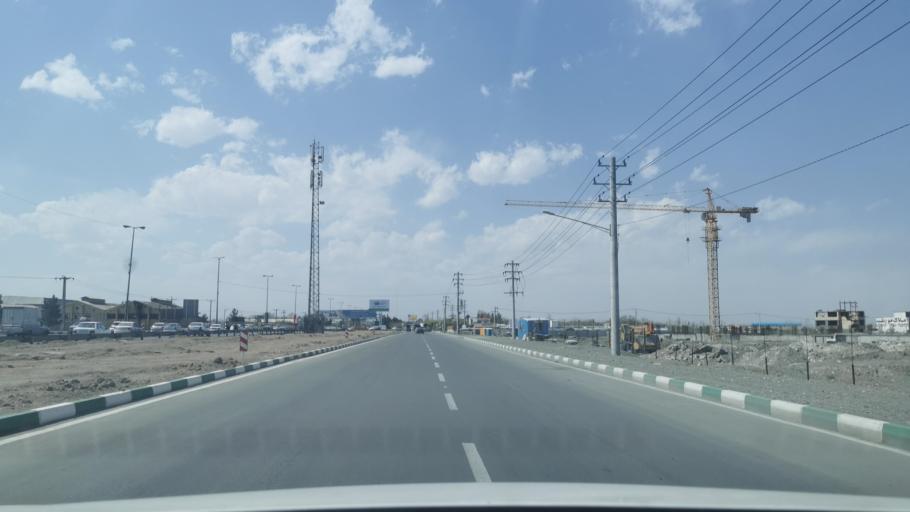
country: IR
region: Razavi Khorasan
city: Mashhad
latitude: 36.3970
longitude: 59.4936
